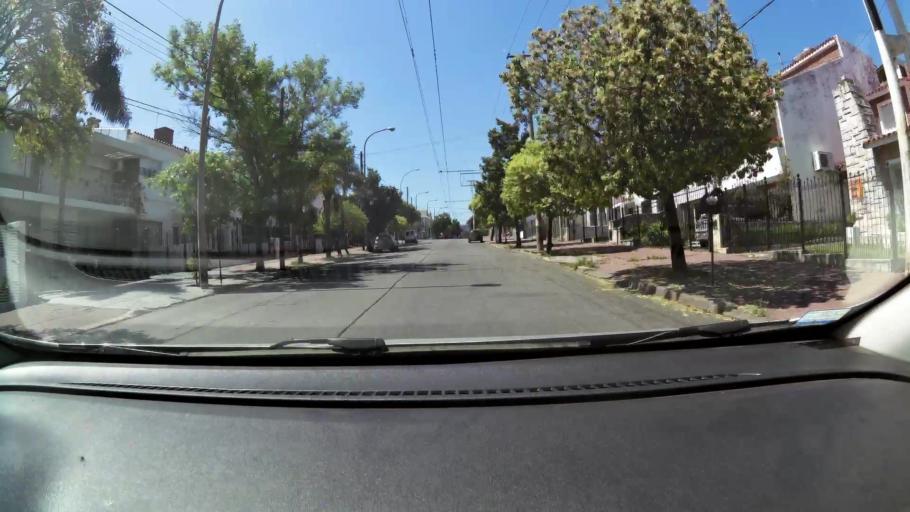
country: AR
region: Cordoba
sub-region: Departamento de Capital
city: Cordoba
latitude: -31.4025
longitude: -64.1871
